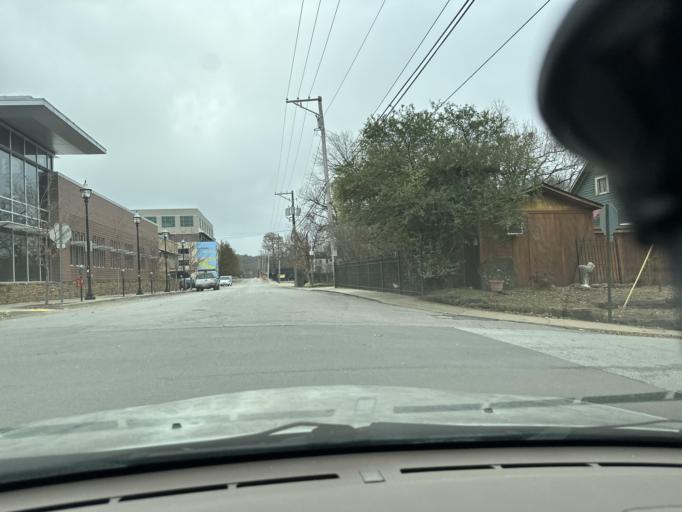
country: US
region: Arkansas
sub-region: Washington County
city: Fayetteville
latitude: 36.0609
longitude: -94.1620
